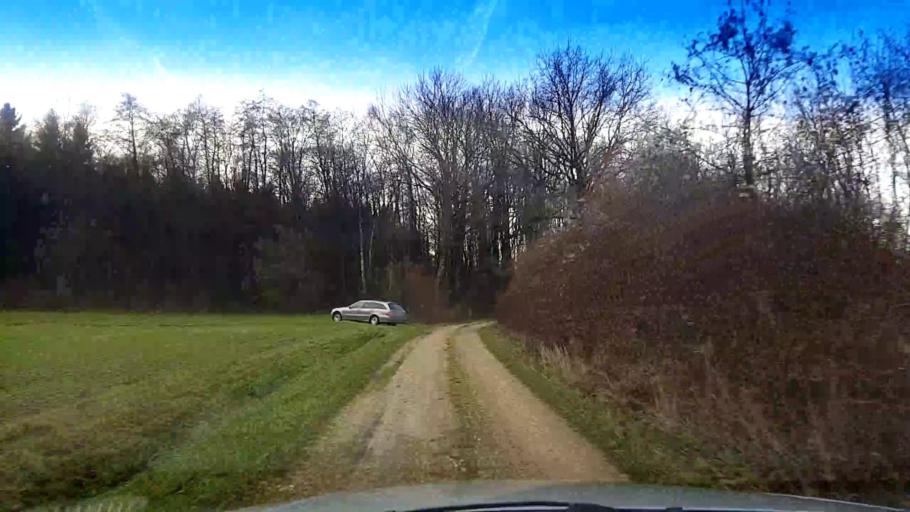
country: DE
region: Bavaria
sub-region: Upper Franconia
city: Schesslitz
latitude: 49.9923
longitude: 11.0316
